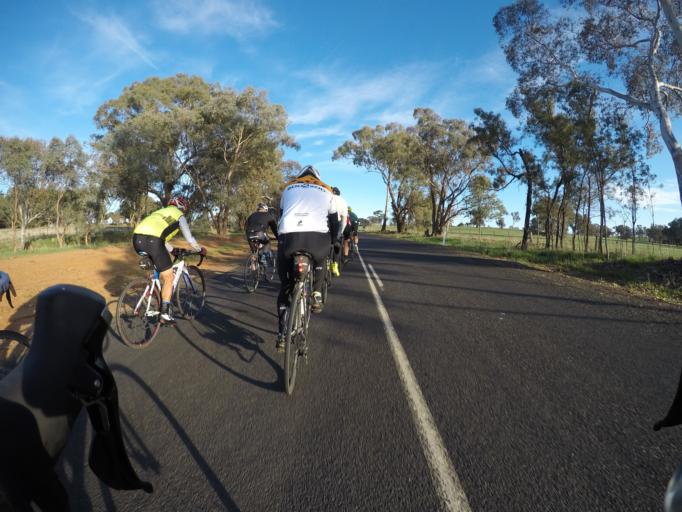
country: AU
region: New South Wales
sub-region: Cabonne
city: Molong
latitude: -33.0105
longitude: 148.7930
